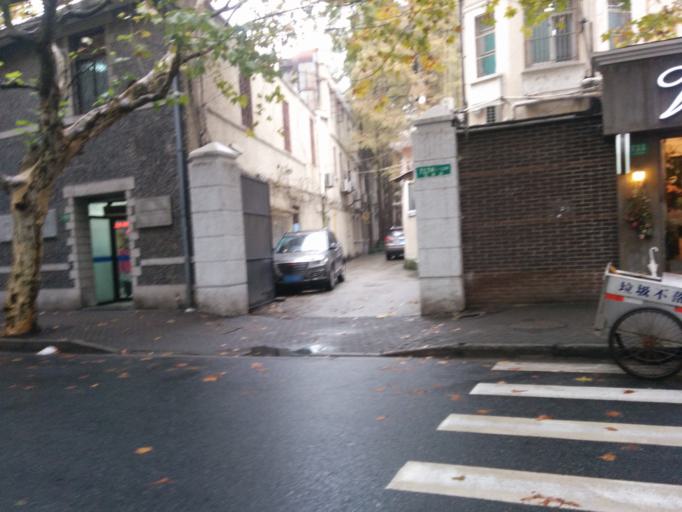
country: CN
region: Shanghai Shi
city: Shanghai
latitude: 31.2227
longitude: 121.4486
